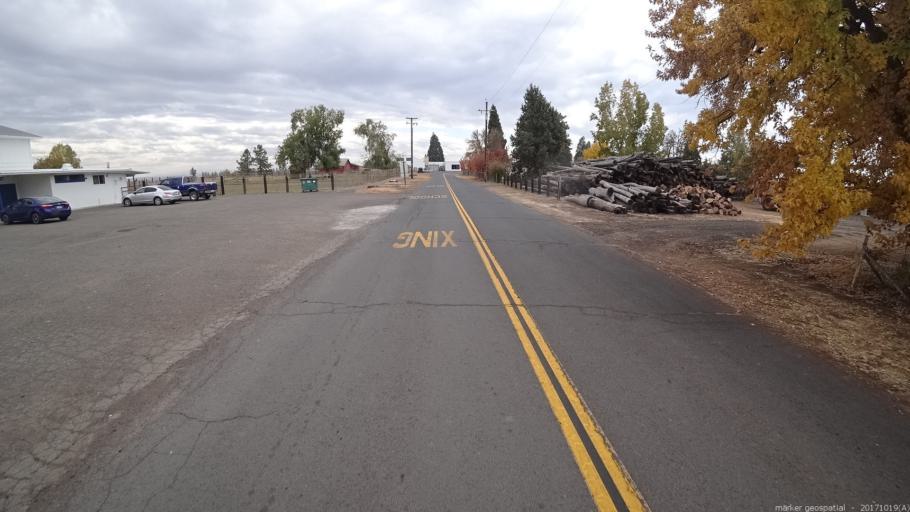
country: US
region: California
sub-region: Shasta County
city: Burney
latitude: 41.0479
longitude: -121.3985
